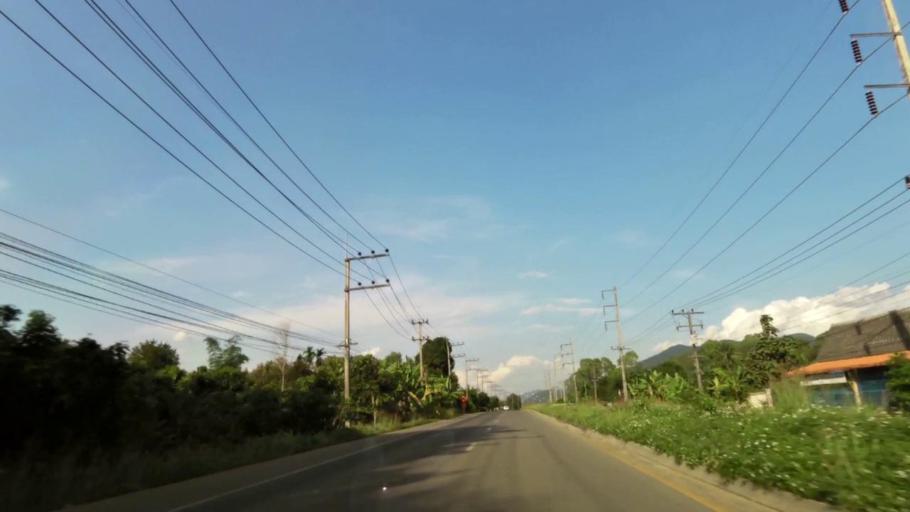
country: TH
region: Chiang Rai
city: Khun Tan
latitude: 19.8757
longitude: 100.2881
